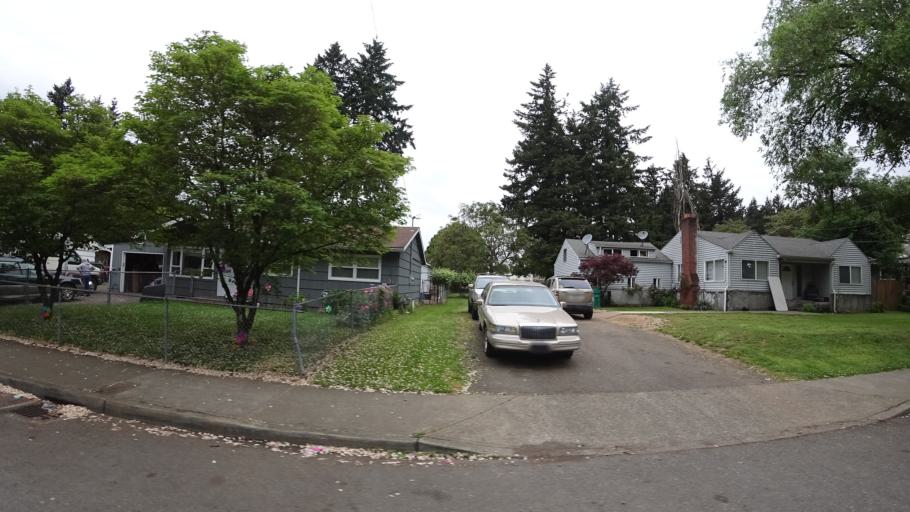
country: US
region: Oregon
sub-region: Multnomah County
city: Lents
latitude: 45.5130
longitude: -122.5210
